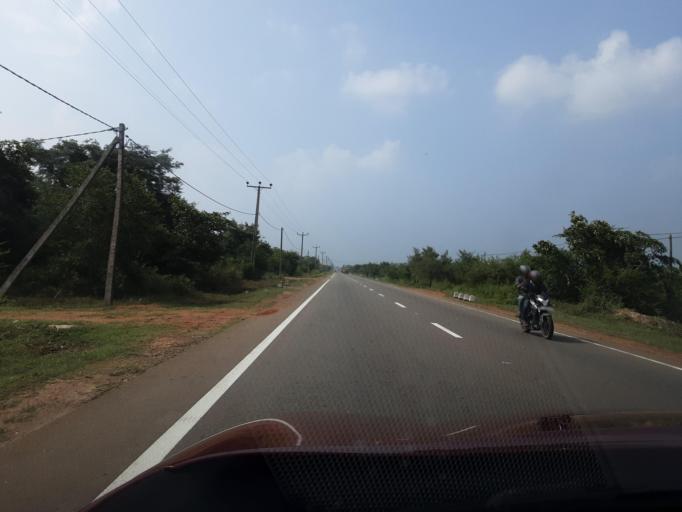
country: LK
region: Northern Province
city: Kilinochchi
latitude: 9.0799
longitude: 80.4833
